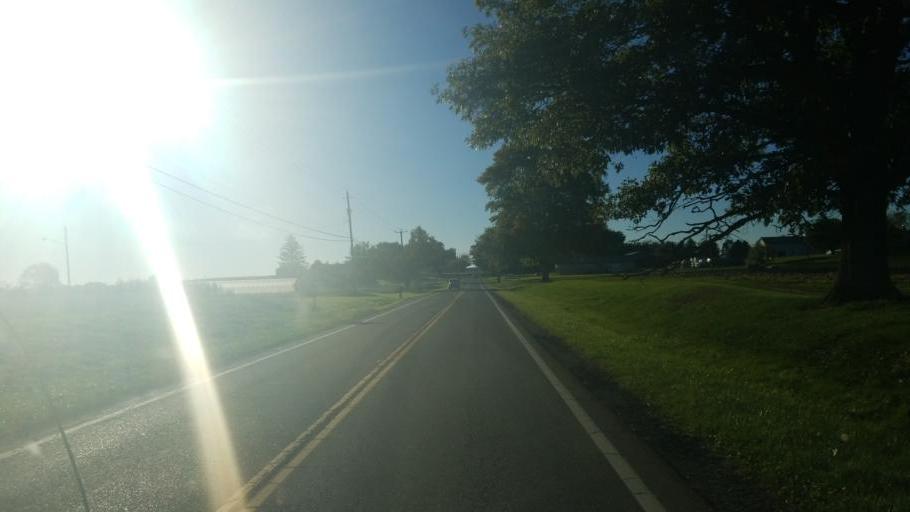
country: US
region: Ohio
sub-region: Columbiana County
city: Leetonia
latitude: 40.9005
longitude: -80.7428
